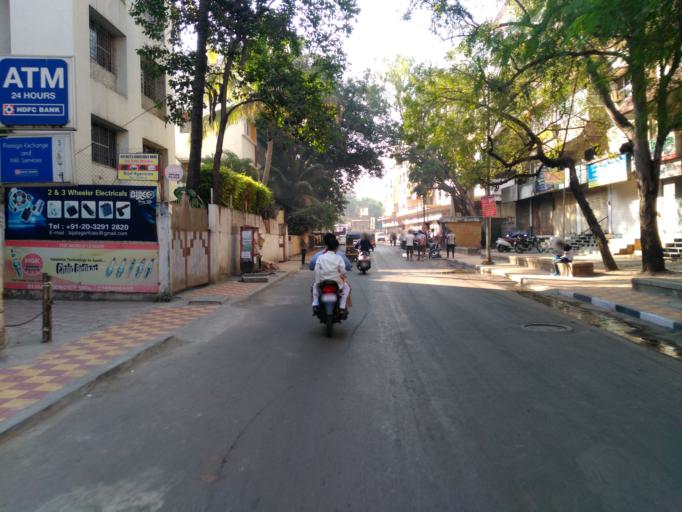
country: IN
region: Maharashtra
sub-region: Pune Division
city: Pune
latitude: 18.5150
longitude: 73.8712
